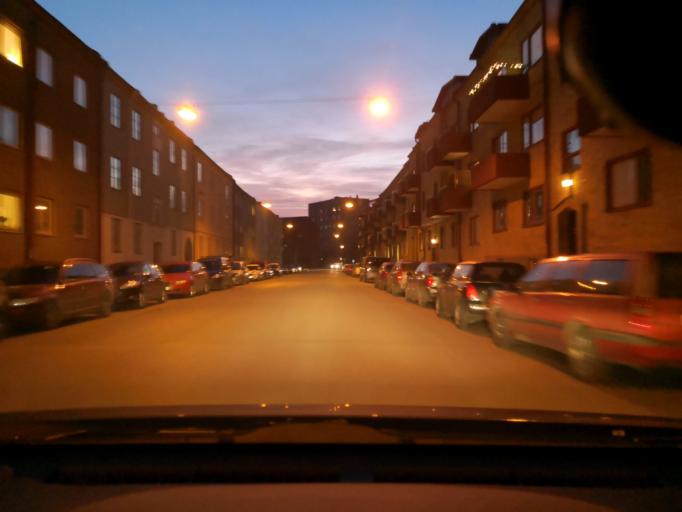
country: SE
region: OErebro
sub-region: Orebro Kommun
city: Orebro
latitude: 59.2840
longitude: 15.2313
